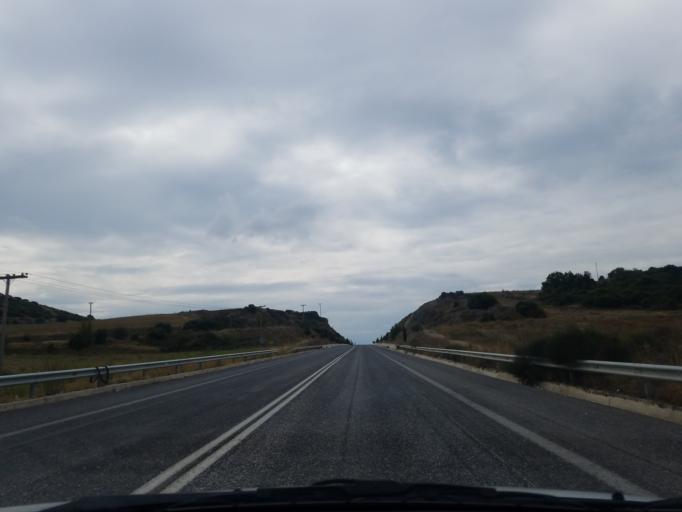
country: GR
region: Central Greece
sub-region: Nomos Fthiotidos
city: Domokos
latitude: 39.1074
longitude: 22.3071
